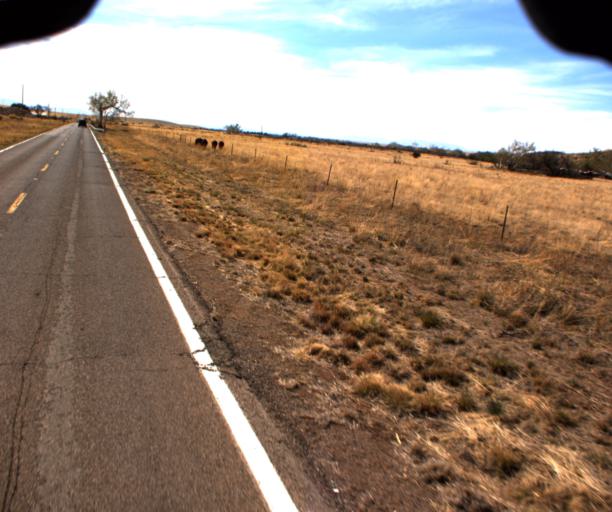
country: US
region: Arizona
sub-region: Cochise County
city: Willcox
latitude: 32.0067
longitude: -109.4016
